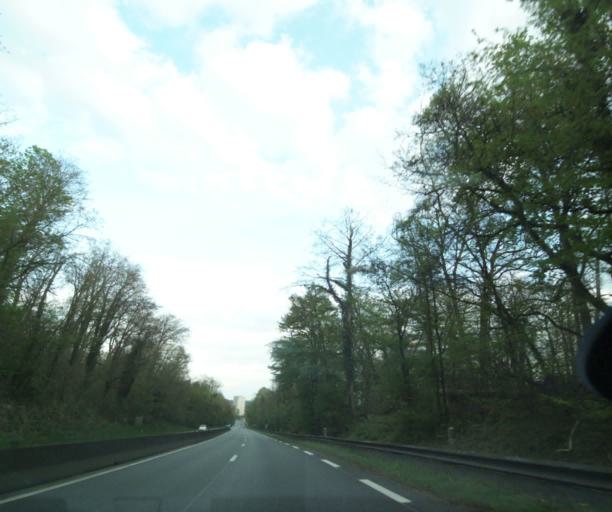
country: FR
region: Ile-de-France
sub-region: Departement de Seine-et-Marne
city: Fontainebleau
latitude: 48.4143
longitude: 2.6773
